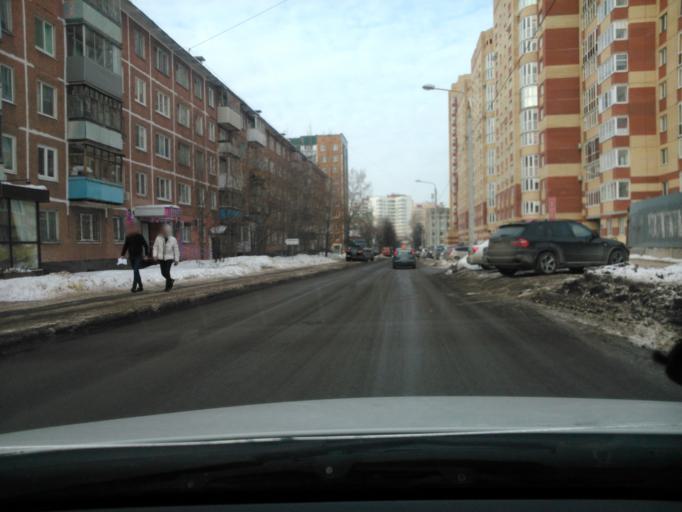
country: RU
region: Perm
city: Perm
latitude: 57.9961
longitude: 56.2408
